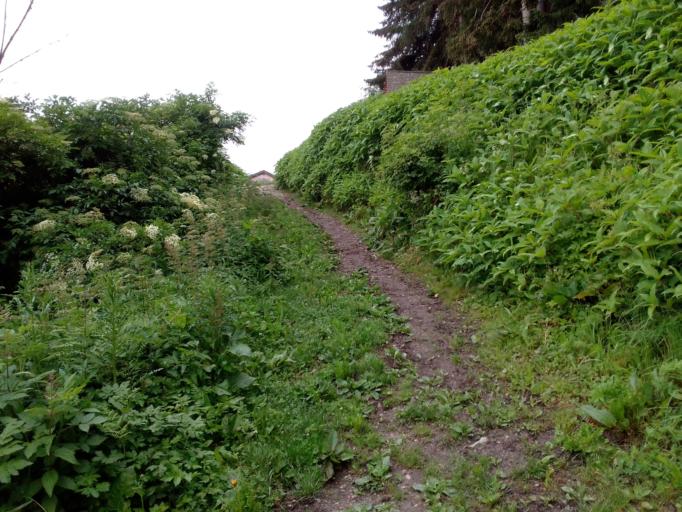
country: IT
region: Trentino-Alto Adige
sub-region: Bolzano
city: Villabassa
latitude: 46.7471
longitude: 12.1689
